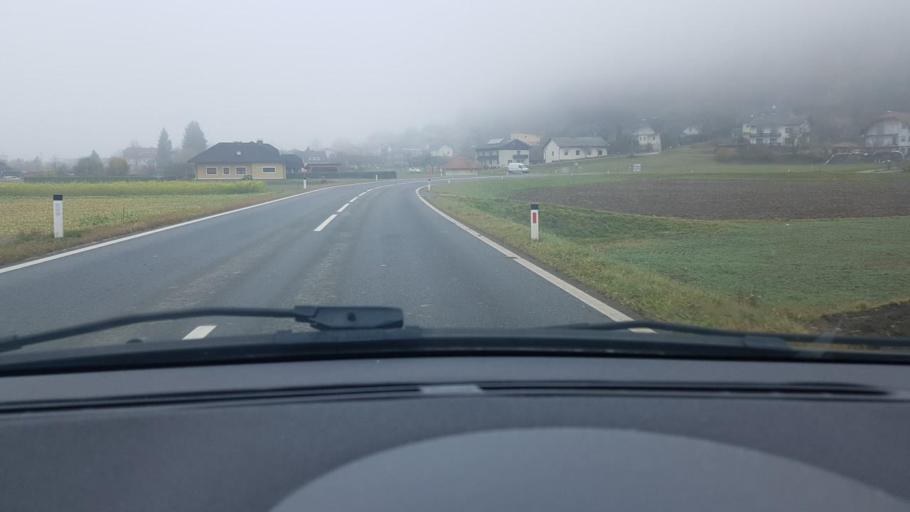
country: AT
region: Carinthia
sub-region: Politischer Bezirk Volkermarkt
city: Sittersdorf
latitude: 46.5488
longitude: 14.6094
